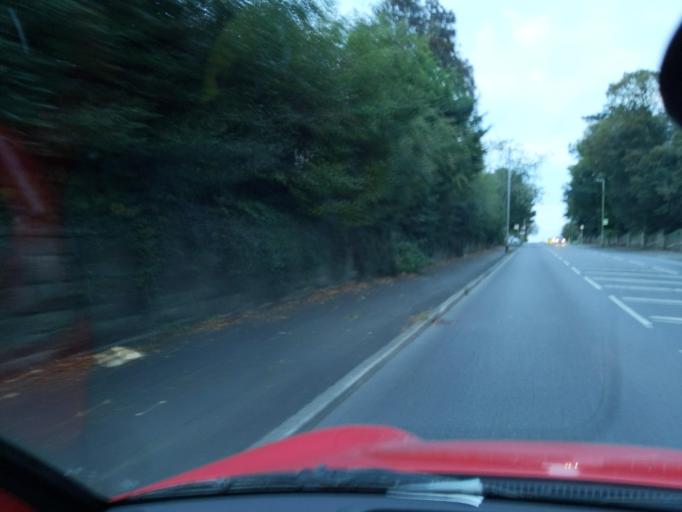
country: GB
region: England
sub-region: Cornwall
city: Millbrook
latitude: 50.3974
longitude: -4.1691
